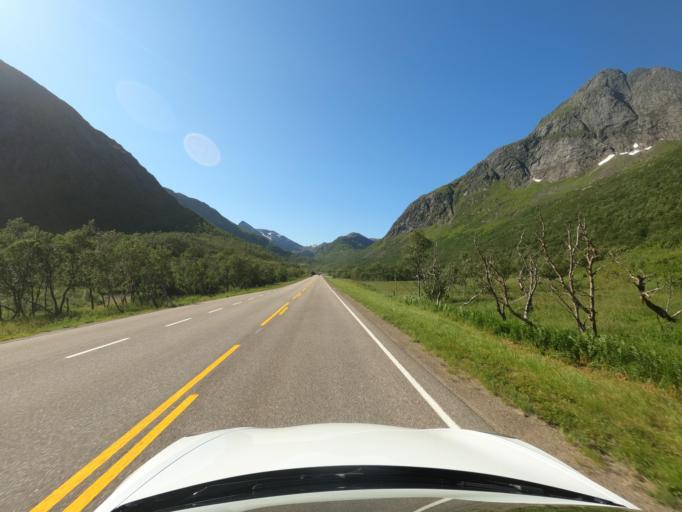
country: NO
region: Nordland
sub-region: Lodingen
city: Lodingen
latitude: 68.5042
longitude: 15.7119
